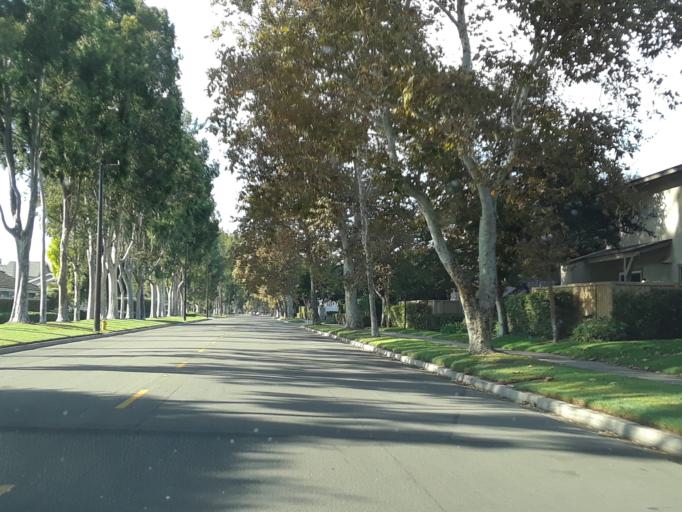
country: US
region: California
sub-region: Orange County
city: Irvine
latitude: 33.6749
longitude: -117.8080
